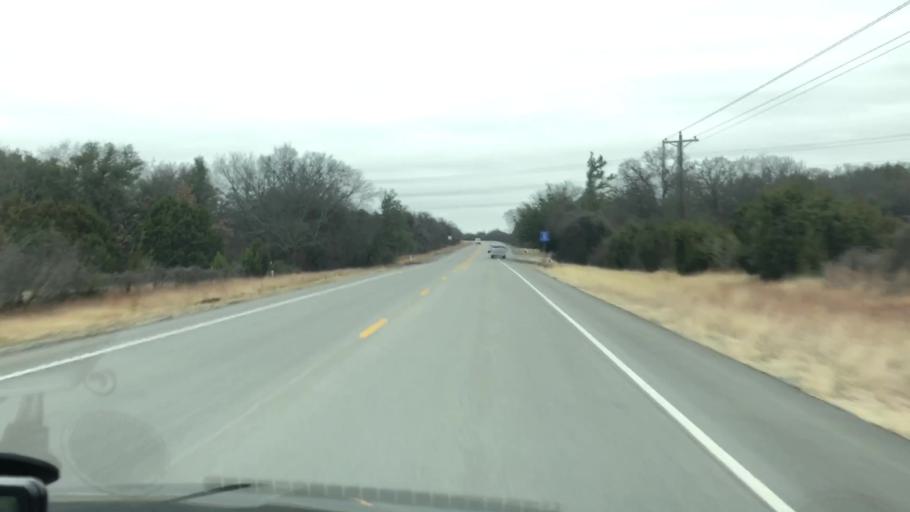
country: US
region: Texas
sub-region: Hamilton County
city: Hico
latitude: 32.0904
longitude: -98.1045
